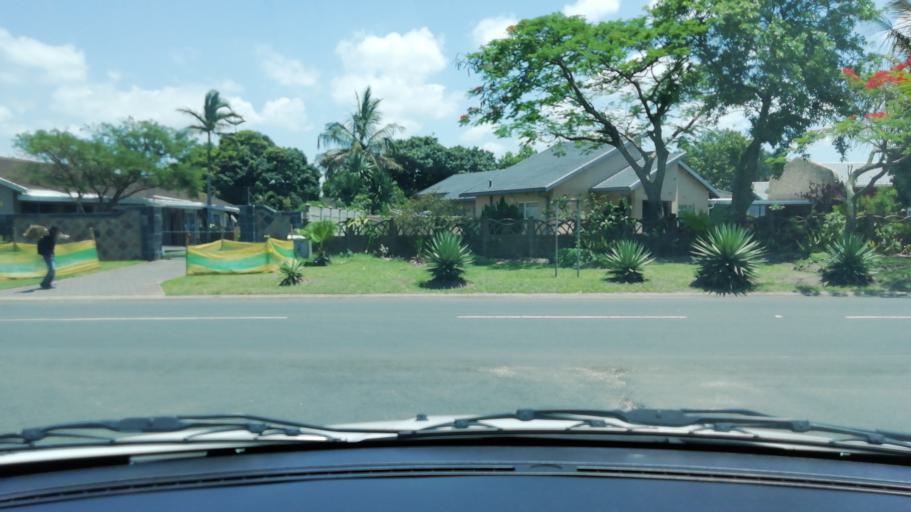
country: ZA
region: KwaZulu-Natal
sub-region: uThungulu District Municipality
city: Richards Bay
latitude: -28.7354
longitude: 32.0598
